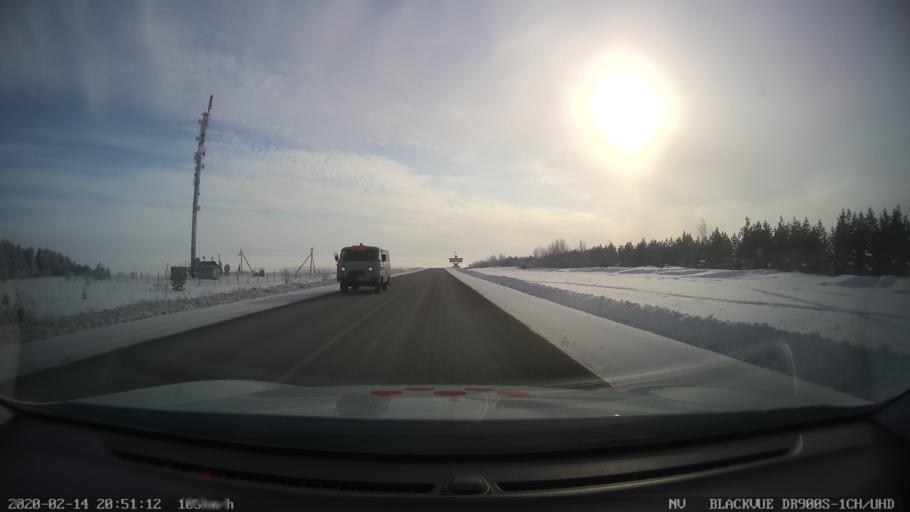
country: RU
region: Tatarstan
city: Kuybyshevskiy Zaton
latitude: 55.2158
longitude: 49.2355
